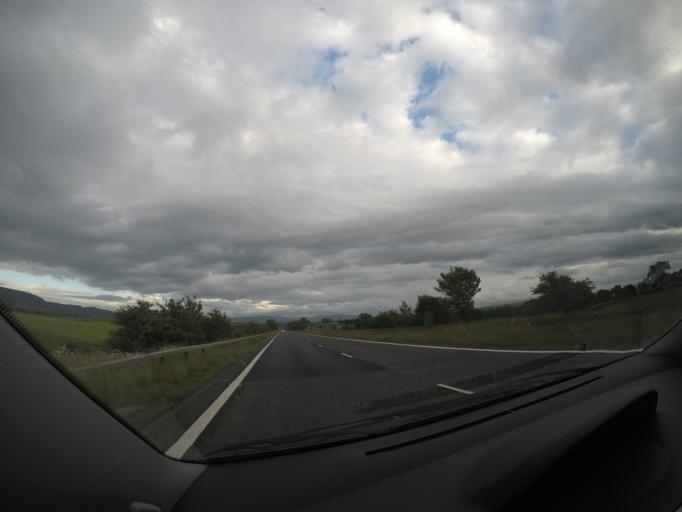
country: GB
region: England
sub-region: Cumbria
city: Appleby-in-Westmorland
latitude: 54.5722
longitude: -2.4631
